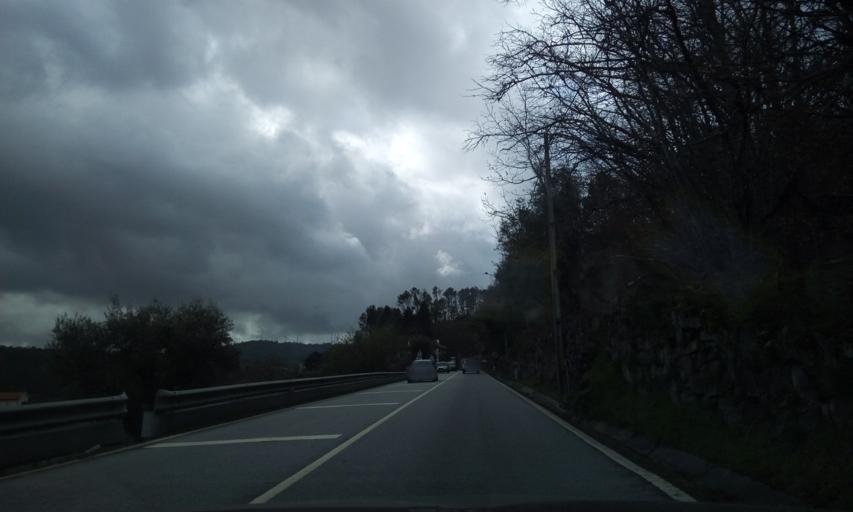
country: PT
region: Viseu
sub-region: Mangualde
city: Mangualde
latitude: 40.6385
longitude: -7.7398
